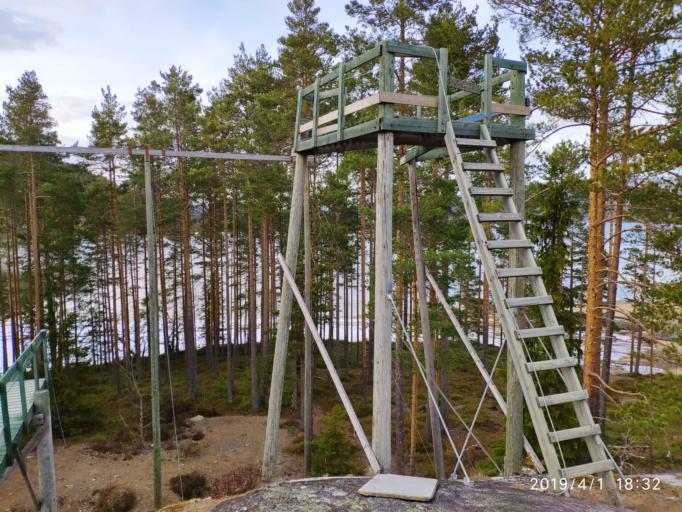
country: NO
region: Telemark
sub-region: Nissedal
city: Treungen
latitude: 59.1181
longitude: 8.4773
